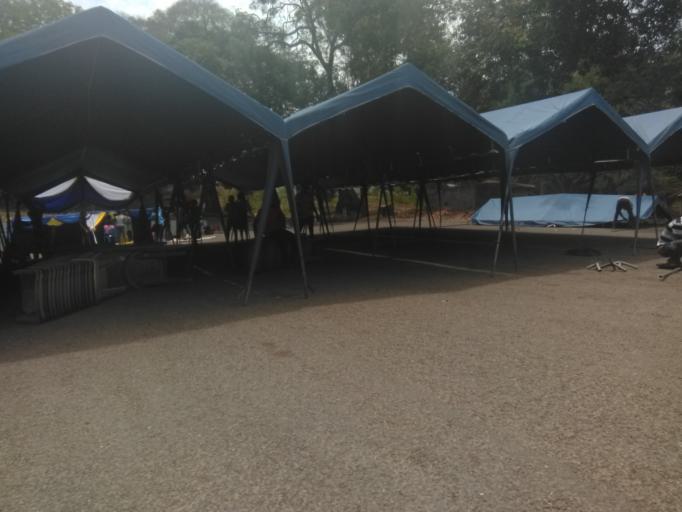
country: GH
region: Central
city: Cape Coast
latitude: 5.1174
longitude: -1.2854
